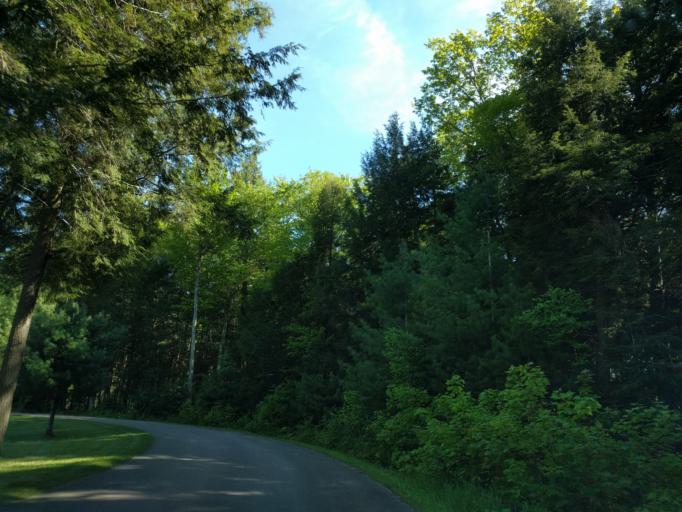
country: US
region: Michigan
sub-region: Marquette County
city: Gwinn
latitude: 46.2571
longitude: -87.3675
